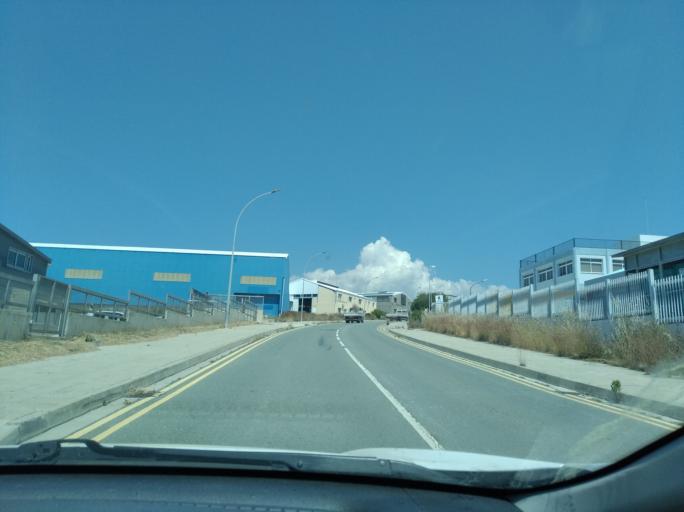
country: CY
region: Limassol
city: Ypsonas
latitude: 34.7279
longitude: 32.9433
